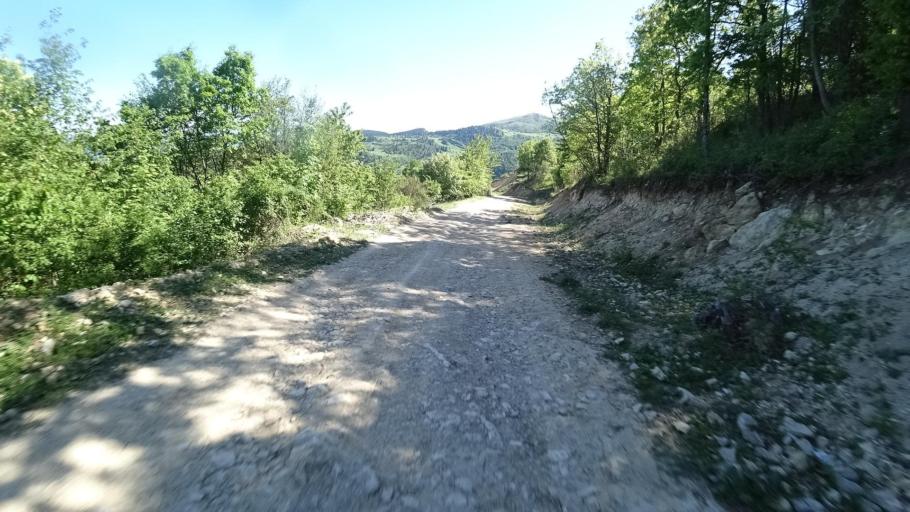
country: BA
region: Federation of Bosnia and Herzegovina
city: Travnik
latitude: 44.2802
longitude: 17.7096
